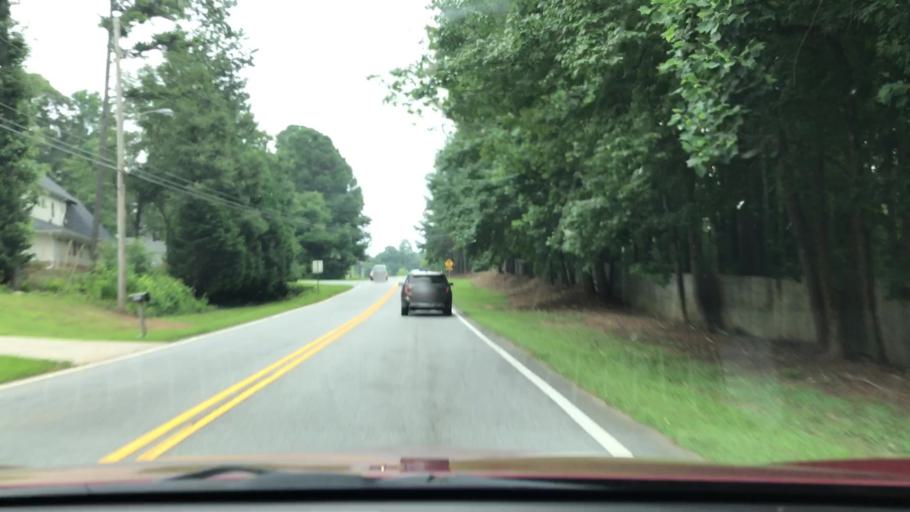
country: US
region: Georgia
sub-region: Gwinnett County
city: Suwanee
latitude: 34.0017
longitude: -84.0434
